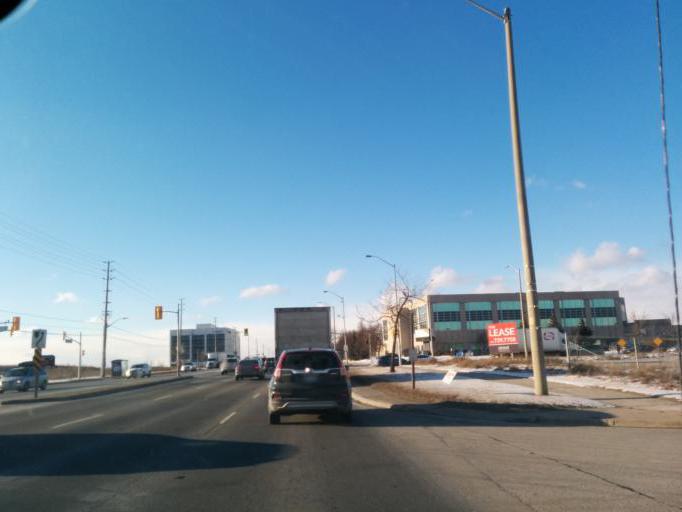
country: CA
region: Ontario
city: Mississauga
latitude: 43.6330
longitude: -79.6883
